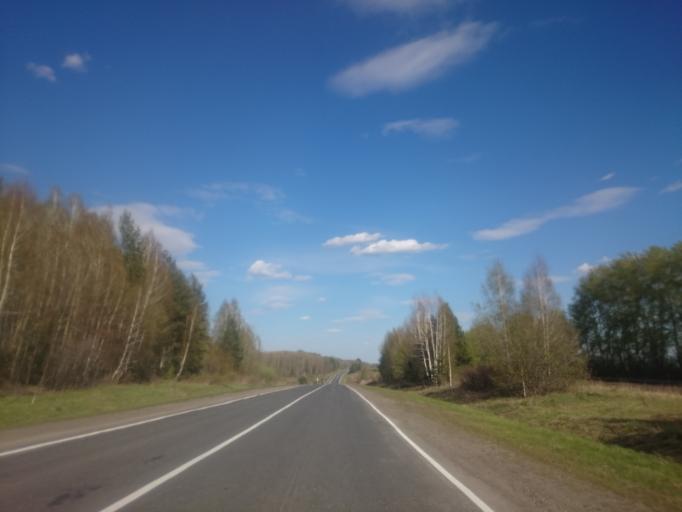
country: RU
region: Sverdlovsk
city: Lesnoy
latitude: 57.6196
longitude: 63.2170
